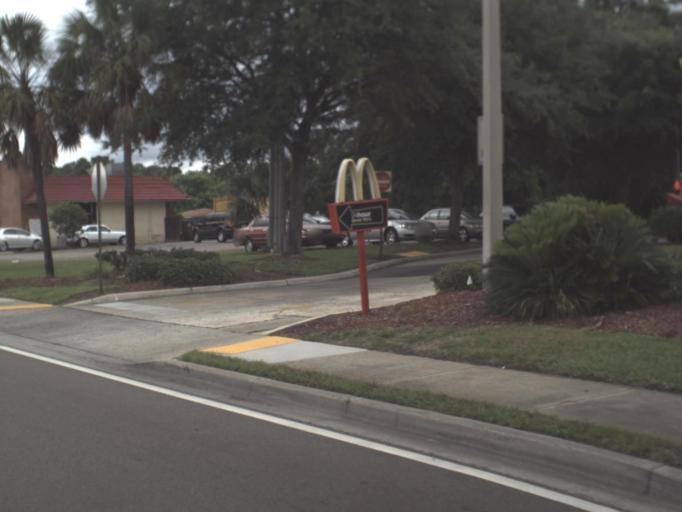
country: US
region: Florida
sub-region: Duval County
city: Jacksonville
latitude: 30.3698
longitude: -81.7236
